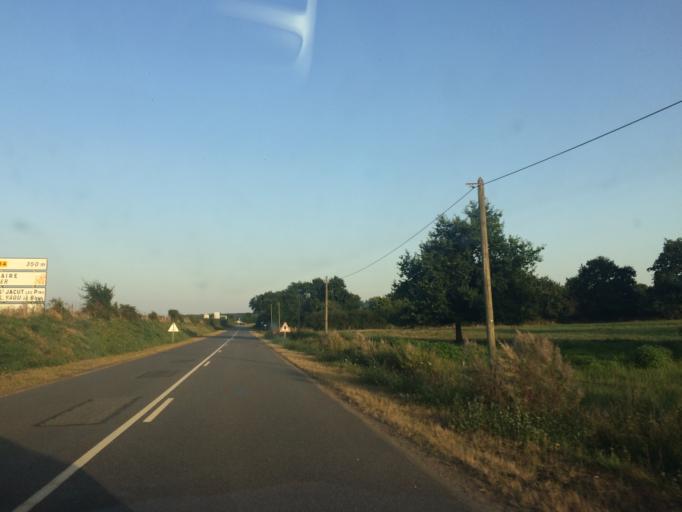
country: FR
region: Brittany
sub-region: Departement du Morbihan
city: Allaire
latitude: 47.6351
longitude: -2.1837
